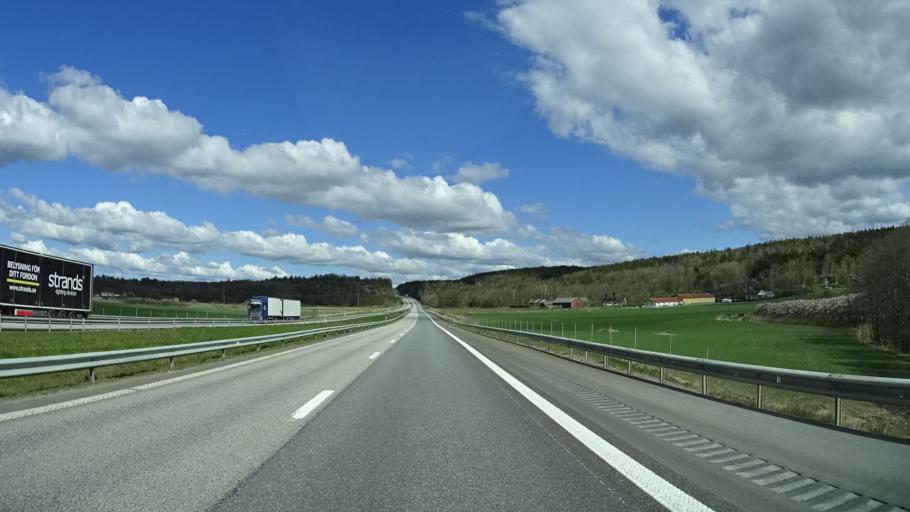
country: SE
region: Halland
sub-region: Kungsbacka Kommun
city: Frillesas
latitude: 57.2978
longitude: 12.2158
